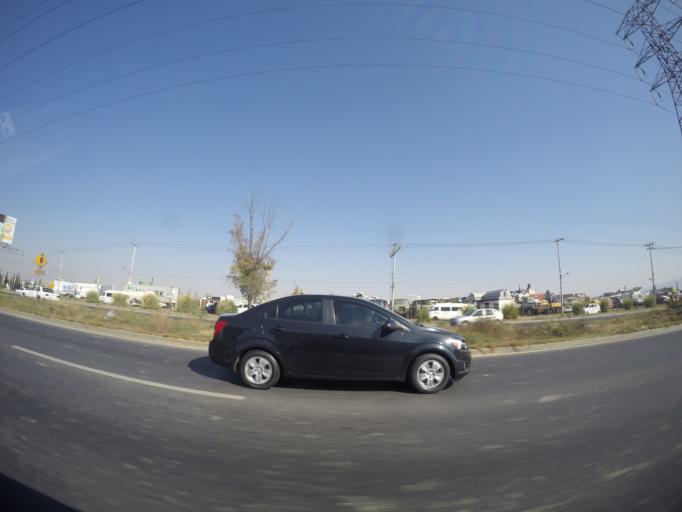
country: MX
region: Mexico
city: Santo Tomas Chiconautla
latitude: 19.6155
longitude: -99.0238
